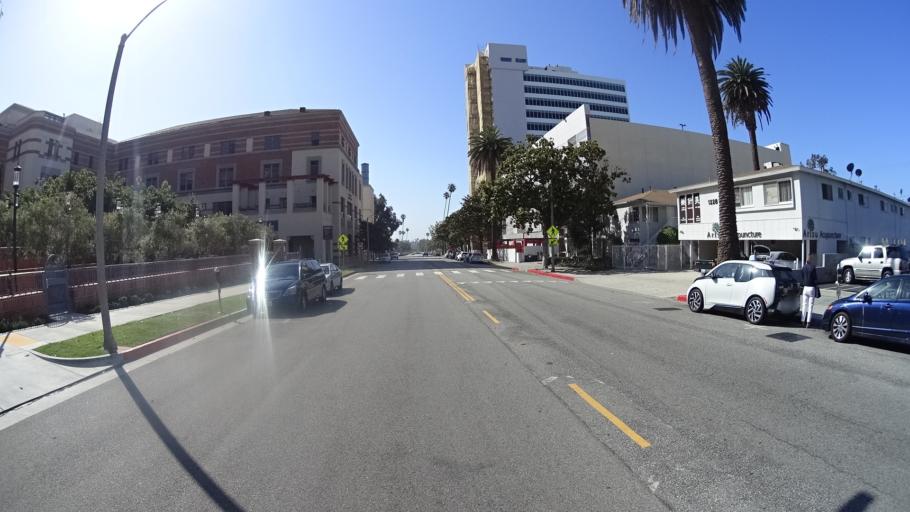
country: US
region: California
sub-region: Los Angeles County
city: Santa Monica
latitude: 34.0270
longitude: -118.4873
